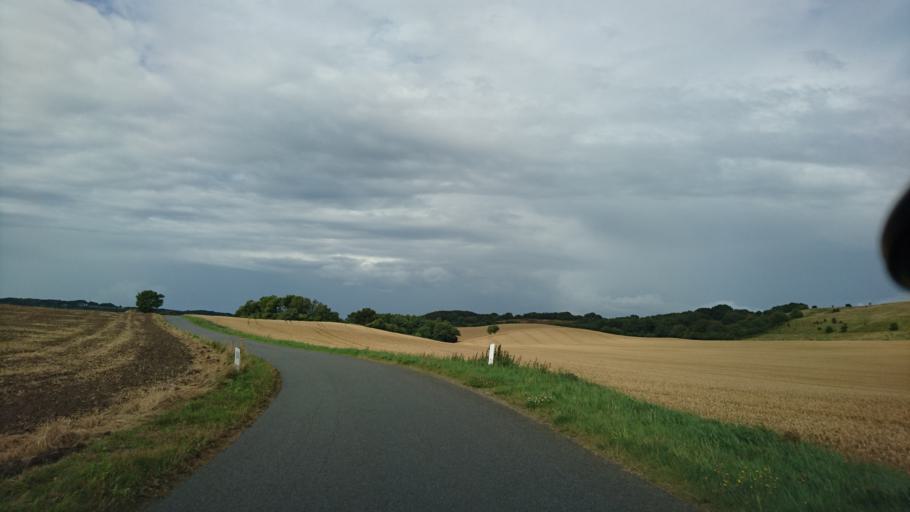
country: DK
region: North Denmark
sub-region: Frederikshavn Kommune
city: Saeby
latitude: 57.3899
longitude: 10.4778
